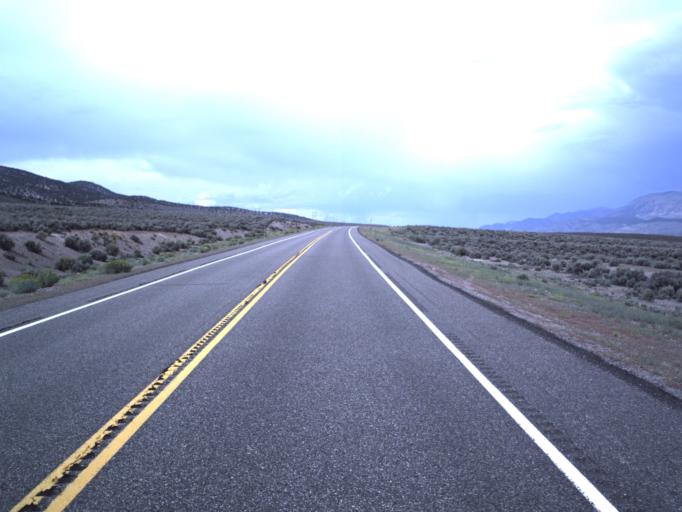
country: US
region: Utah
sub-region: Piute County
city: Junction
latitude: 38.2946
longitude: -112.2252
